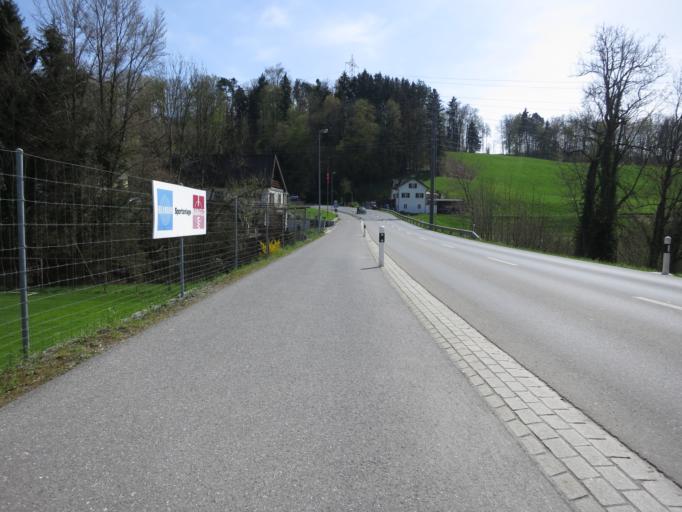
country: CH
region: Zurich
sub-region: Bezirk Hinwil
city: Rueti / Oberdorf
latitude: 47.2440
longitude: 8.8853
